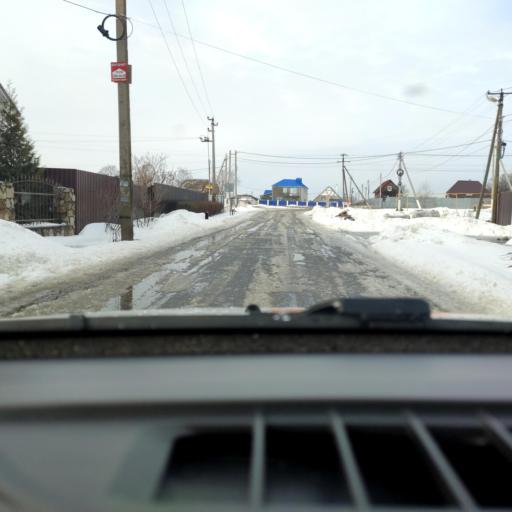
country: RU
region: Voronezj
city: Podgornoye
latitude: 51.7735
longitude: 39.1262
